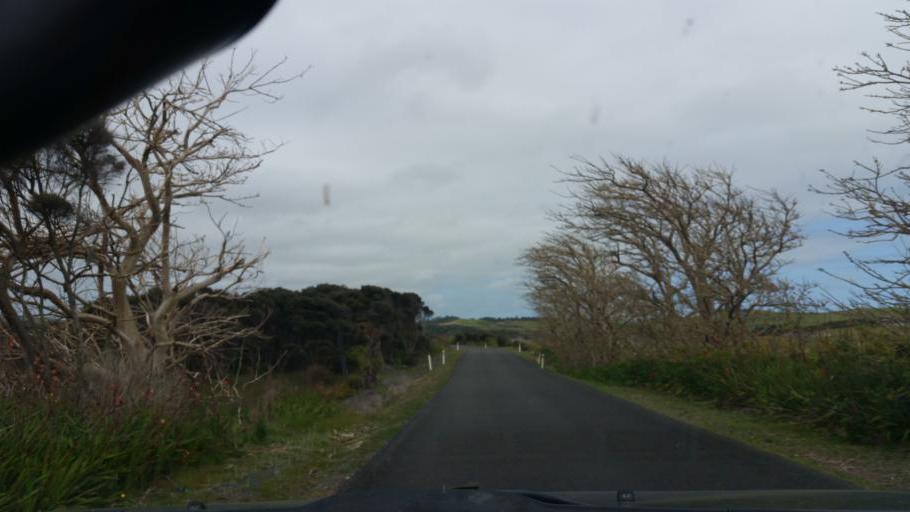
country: NZ
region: Northland
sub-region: Kaipara District
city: Dargaville
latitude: -35.8038
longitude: 173.6319
